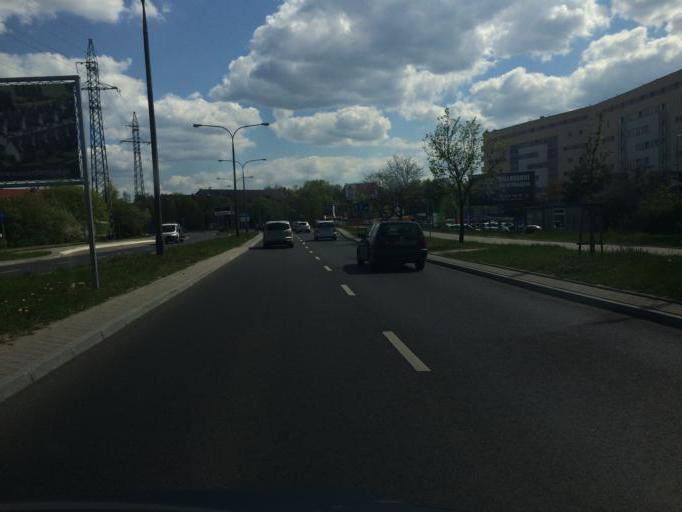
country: PL
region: Warmian-Masurian Voivodeship
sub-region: Olsztyn
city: Kortowo
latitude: 53.7700
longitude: 20.4581
